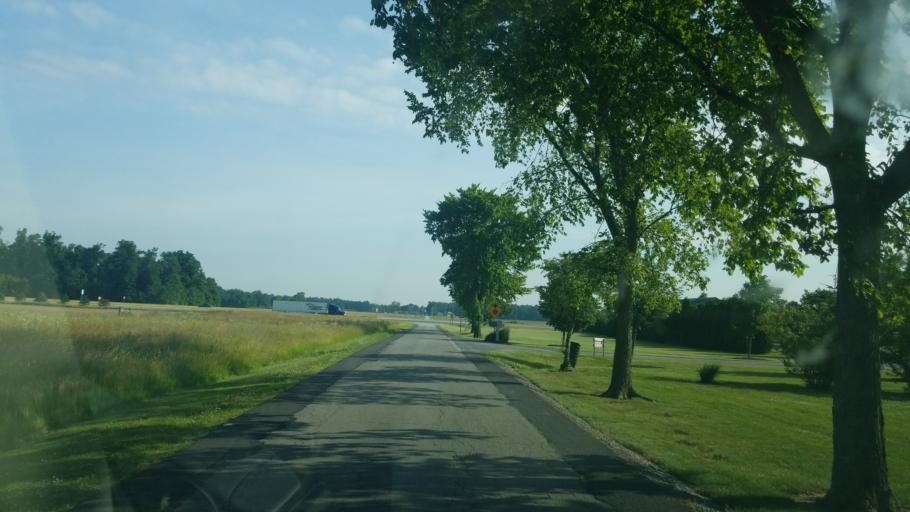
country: US
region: Ohio
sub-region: Hancock County
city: Arlington
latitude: 40.8250
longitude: -83.6705
